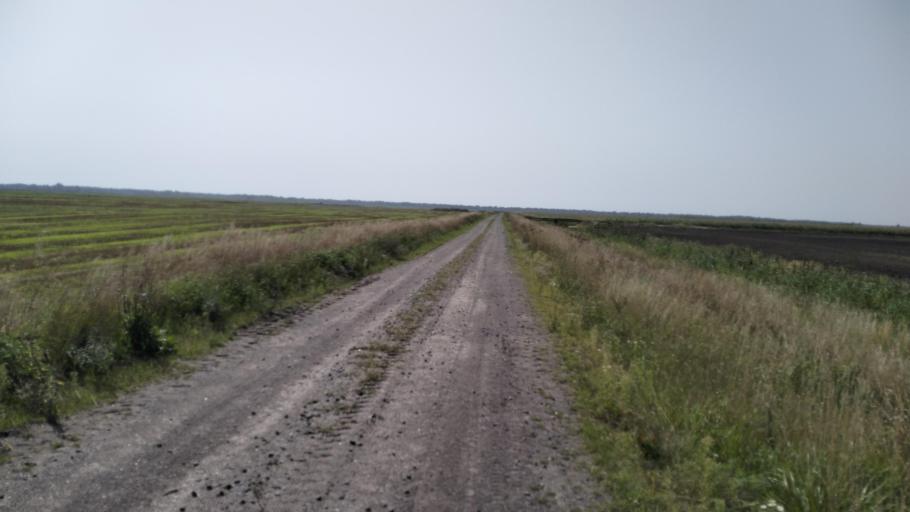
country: BY
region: Brest
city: Davyd-Haradok
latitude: 51.9946
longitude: 27.1648
